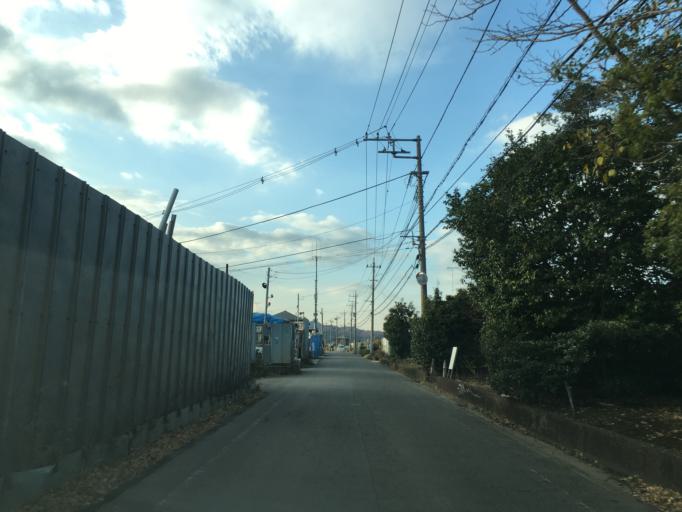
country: JP
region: Kanagawa
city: Zama
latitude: 35.5381
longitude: 139.3507
